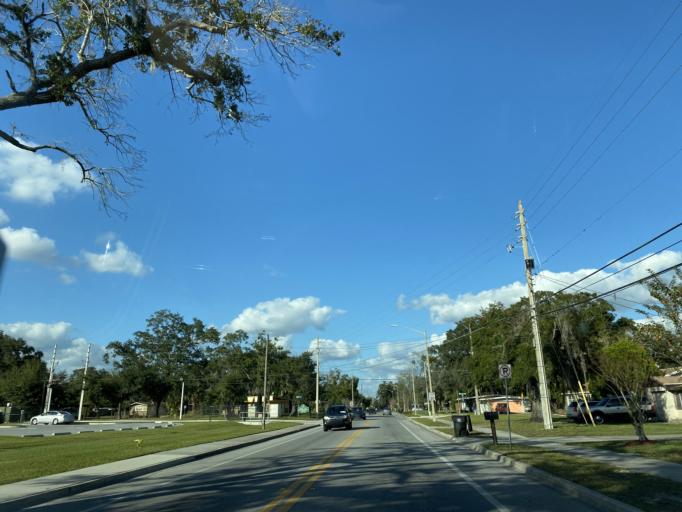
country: US
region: Florida
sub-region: Orange County
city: Orlando
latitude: 28.5485
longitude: -81.4056
